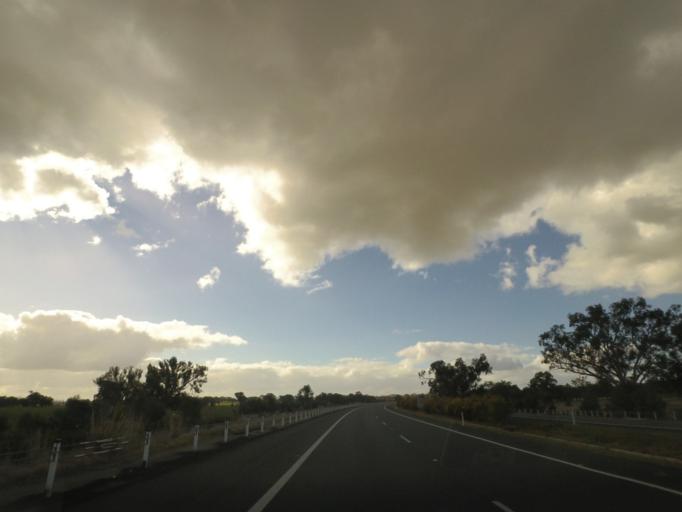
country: AU
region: New South Wales
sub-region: Greater Hume Shire
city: Holbrook
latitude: -35.7153
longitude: 147.3030
